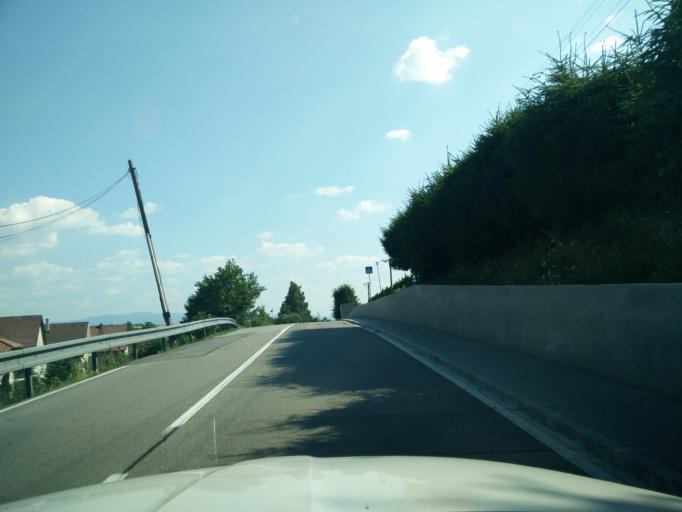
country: SK
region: Nitriansky
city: Bojnice
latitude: 48.8296
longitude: 18.4777
